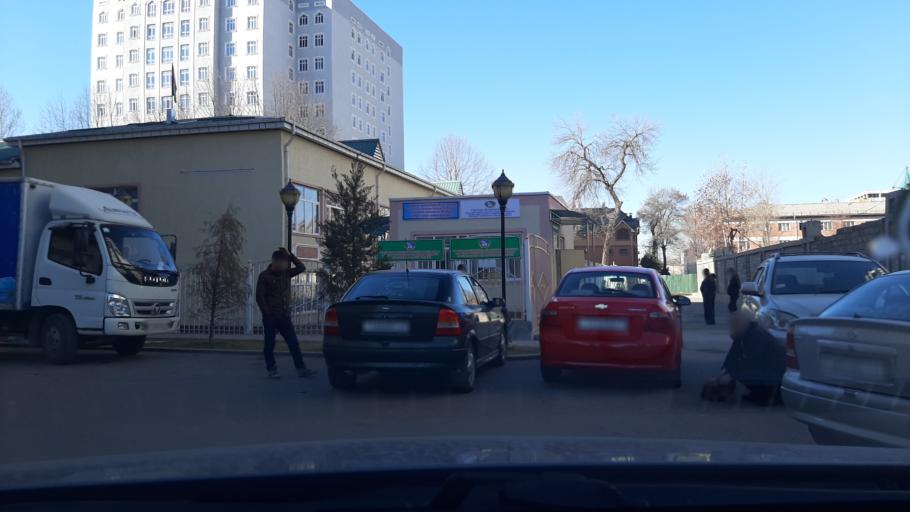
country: TJ
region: Dushanbe
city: Dushanbe
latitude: 38.5965
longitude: 68.7862
